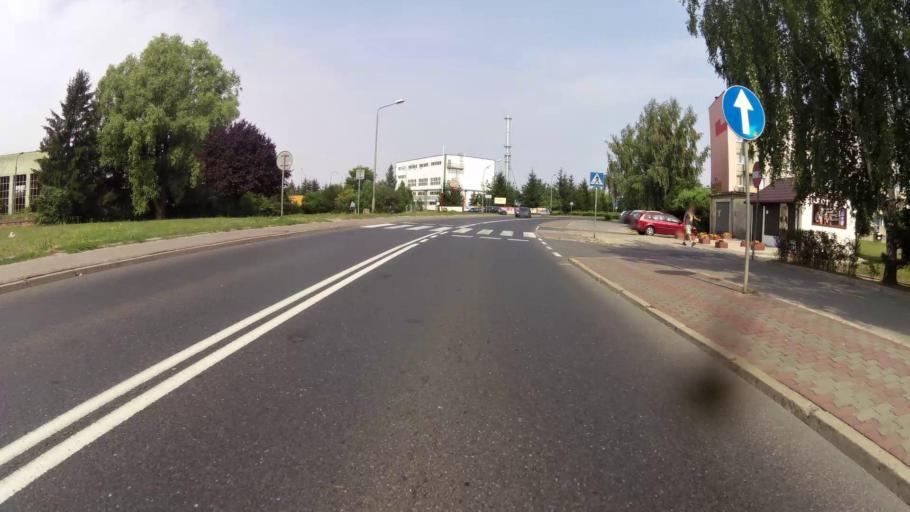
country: PL
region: West Pomeranian Voivodeship
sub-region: Powiat mysliborski
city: Mysliborz
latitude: 52.9269
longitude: 14.8757
